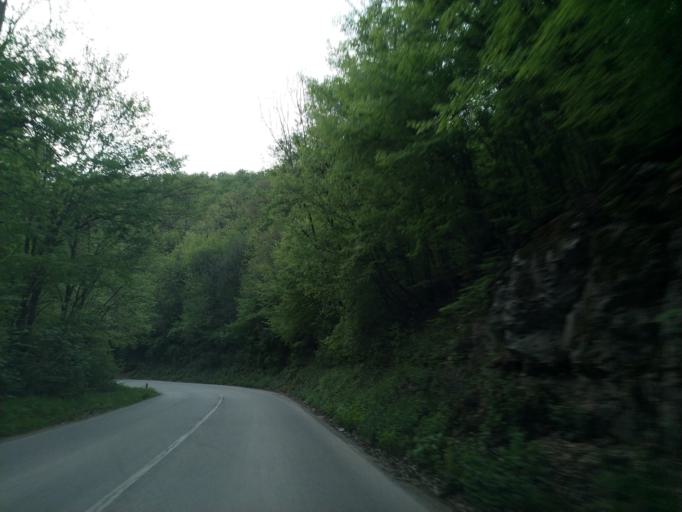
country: RS
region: Central Serbia
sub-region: Pomoravski Okrug
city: Despotovac
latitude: 43.9683
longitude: 21.5278
